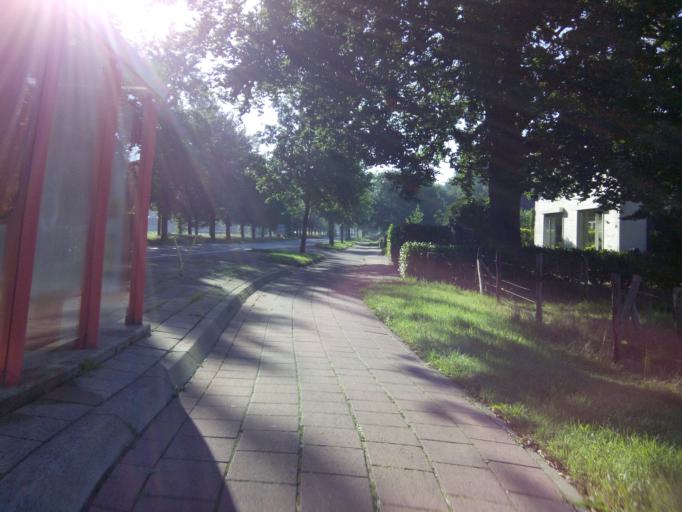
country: NL
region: Utrecht
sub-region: Gemeente Utrechtse Heuvelrug
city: Leersum
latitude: 52.0064
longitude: 5.4408
